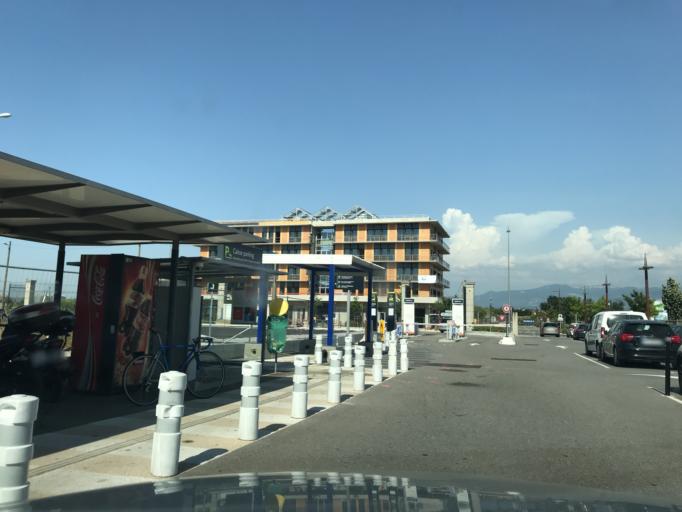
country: FR
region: Rhone-Alpes
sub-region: Departement de la Drome
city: Saint-Marcel-les-Valence
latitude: 44.9919
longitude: 4.9791
